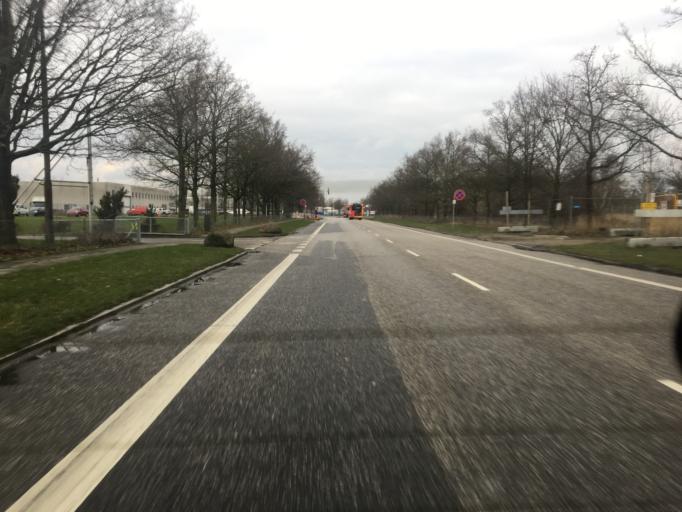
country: DK
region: Capital Region
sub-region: Hvidovre Kommune
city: Hvidovre
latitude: 55.6113
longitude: 12.4902
